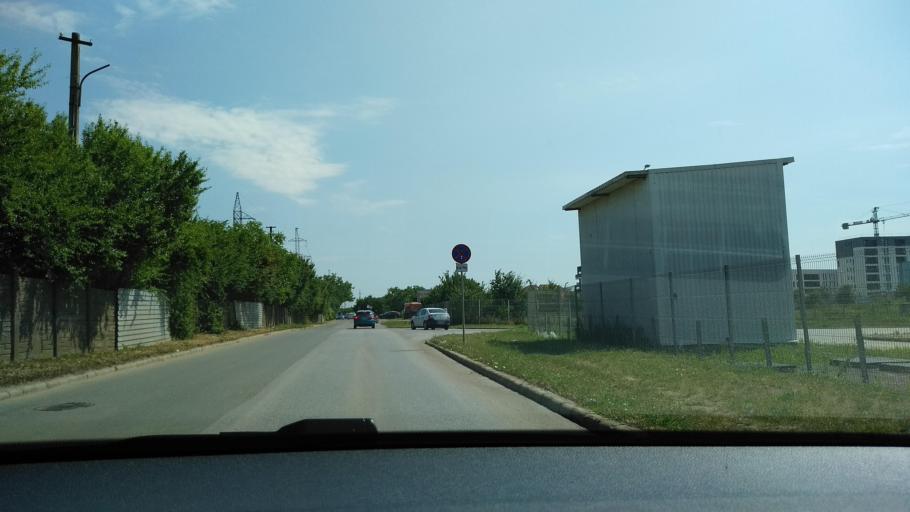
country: RO
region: Timis
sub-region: Comuna Dumbravita
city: Dumbravita
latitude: 45.7886
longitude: 21.2205
